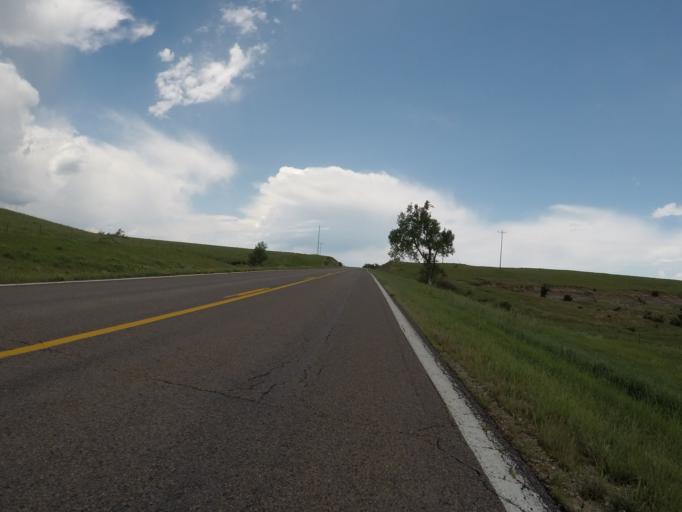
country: US
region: Kansas
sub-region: Wabaunsee County
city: Alma
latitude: 38.8690
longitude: -96.3289
